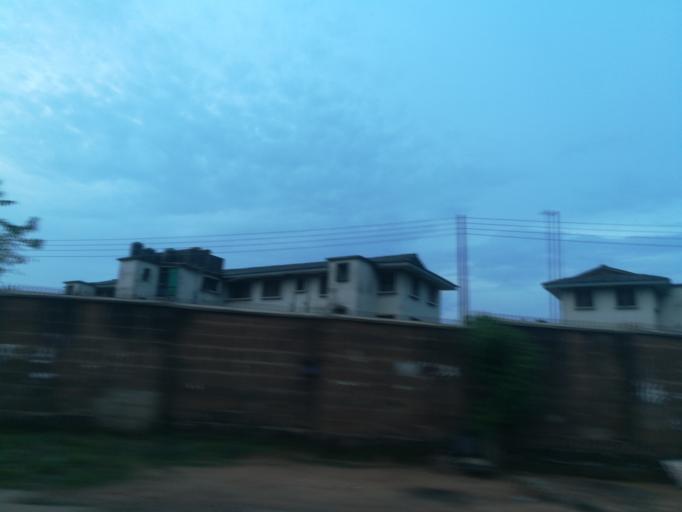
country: NG
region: Oyo
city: Ibadan
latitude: 7.3991
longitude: 3.9092
